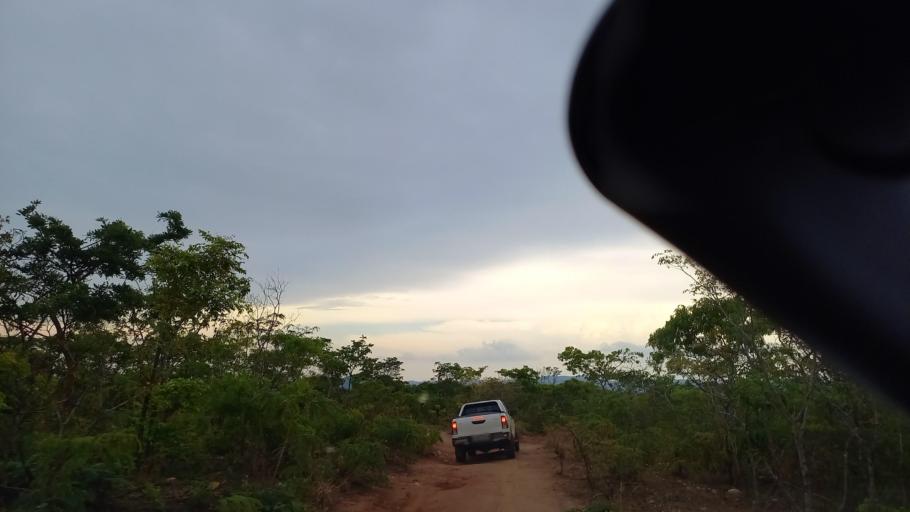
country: ZM
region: Lusaka
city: Kafue
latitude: -16.0486
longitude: 28.3326
